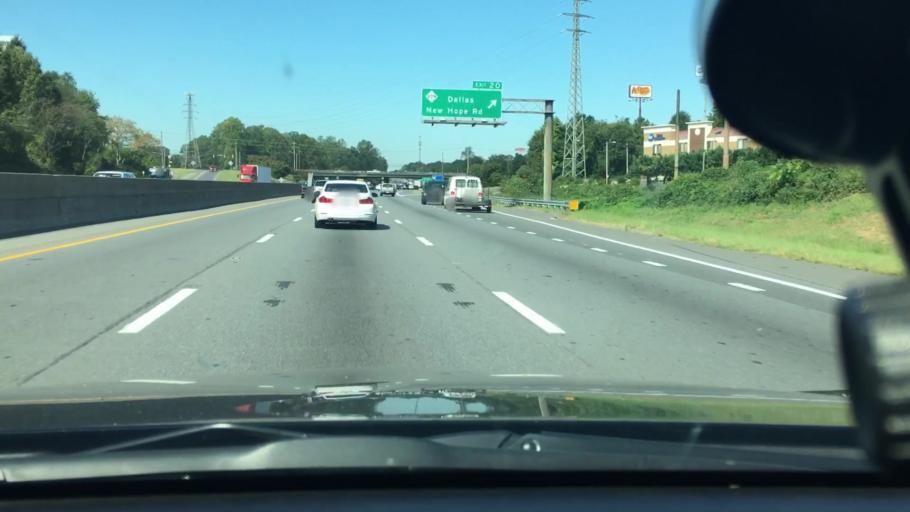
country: US
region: North Carolina
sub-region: Gaston County
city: Ranlo
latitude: 35.2674
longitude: -81.1456
